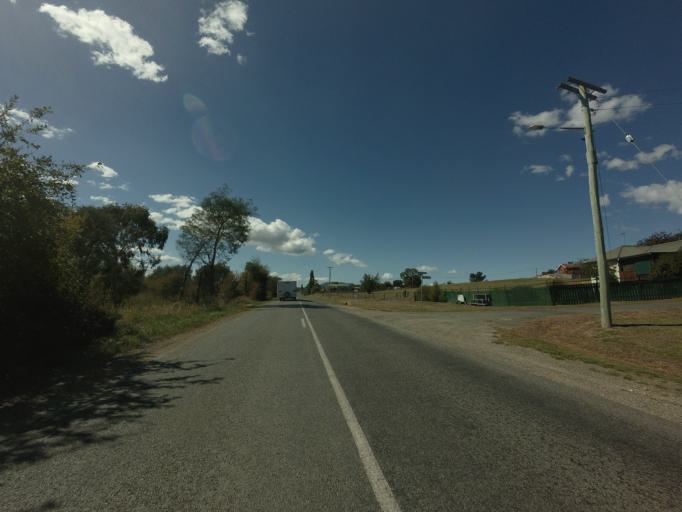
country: AU
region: Tasmania
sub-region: Break O'Day
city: St Helens
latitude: -41.6438
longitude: 147.9617
